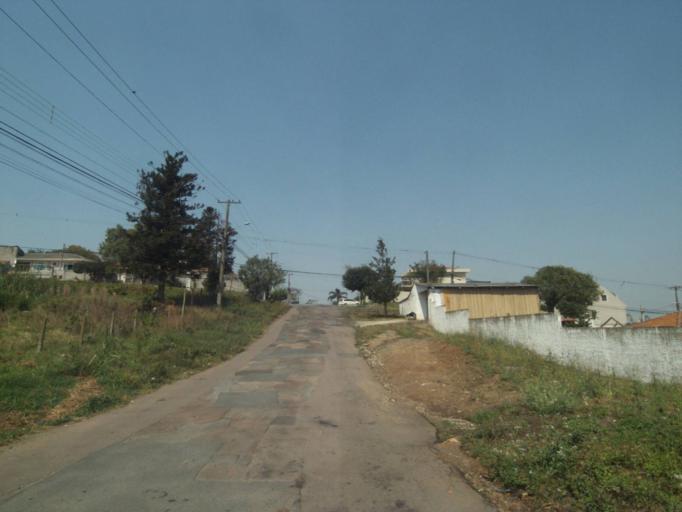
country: BR
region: Parana
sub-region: Sao Jose Dos Pinhais
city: Sao Jose dos Pinhais
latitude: -25.5055
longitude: -49.2752
